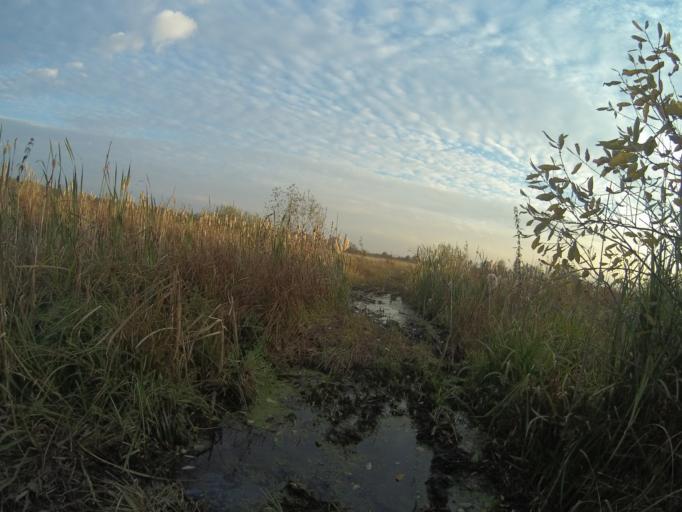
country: RU
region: Vladimir
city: Kommunar
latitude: 56.1053
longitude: 40.4277
